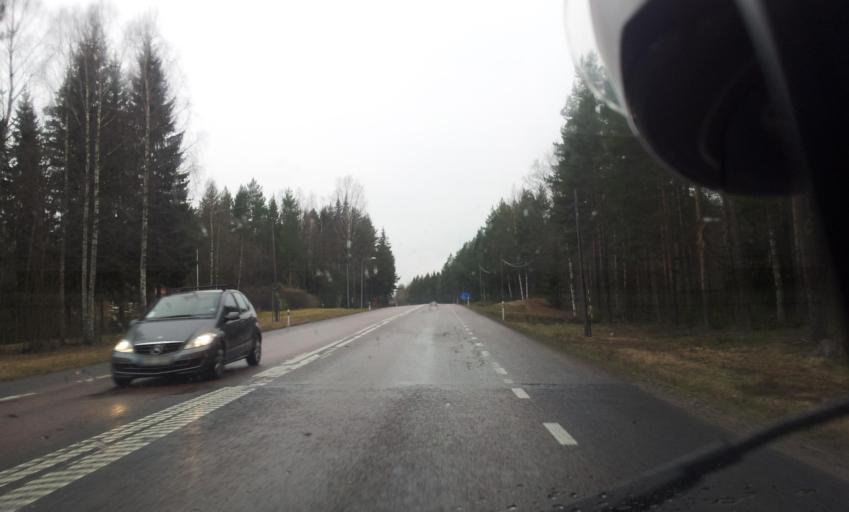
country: SE
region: Dalarna
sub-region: Borlange Kommun
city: Borlaenge
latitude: 60.5295
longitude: 15.3293
